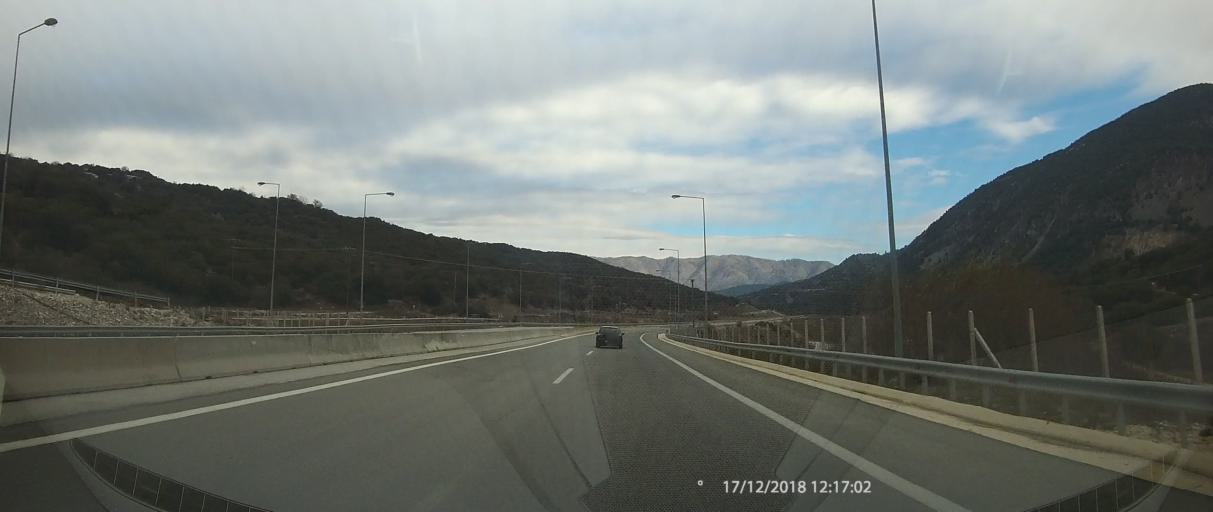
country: GR
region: Epirus
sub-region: Nomos Ioanninon
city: Metsovo
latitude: 39.7363
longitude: 21.0541
